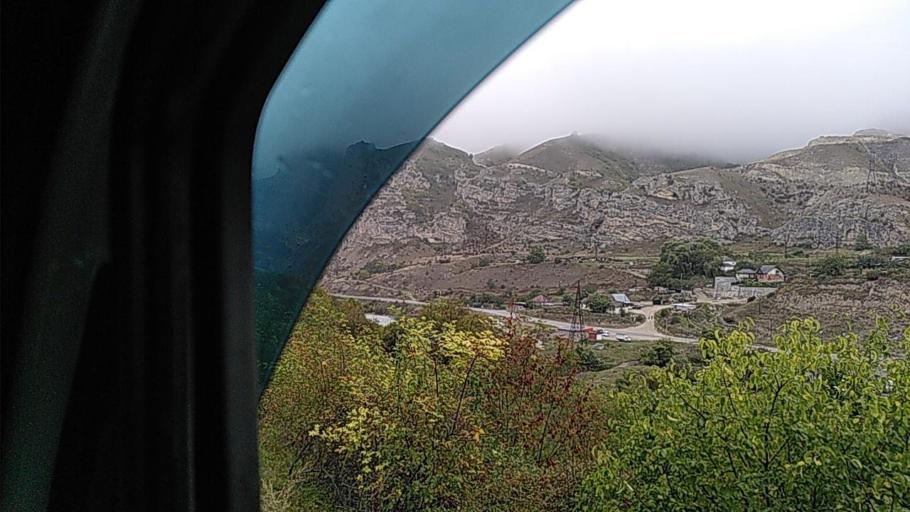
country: RU
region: Kabardino-Balkariya
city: Zhankhoteko
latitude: 43.5084
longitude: 43.1495
